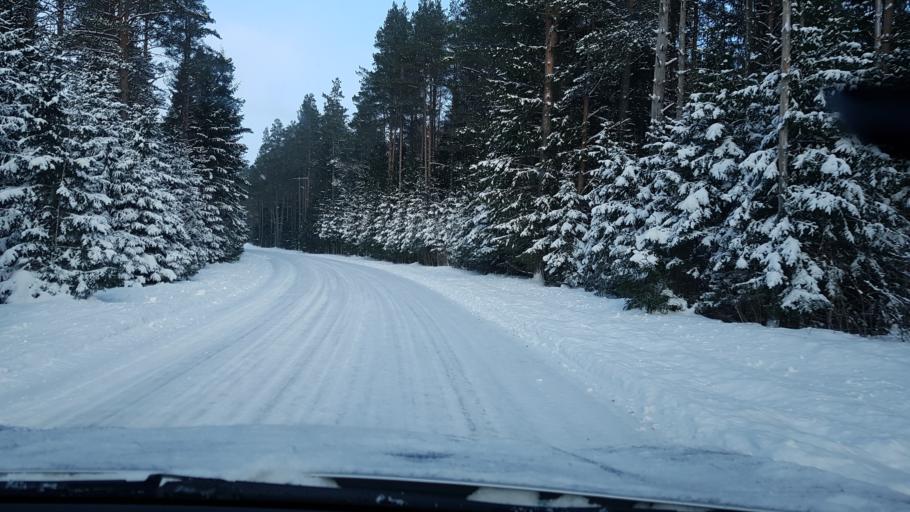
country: EE
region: Harju
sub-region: Nissi vald
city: Turba
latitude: 59.1845
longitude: 24.1411
